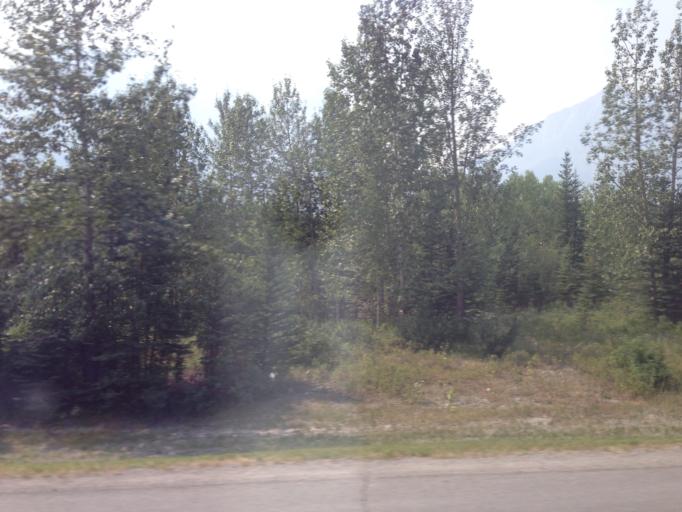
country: CA
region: Alberta
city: Canmore
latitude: 51.0820
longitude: -115.3423
